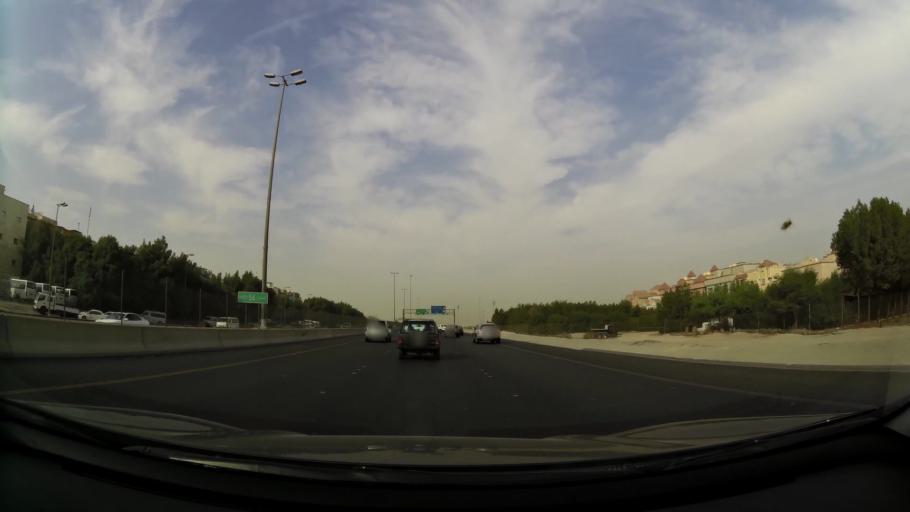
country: KW
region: Al Farwaniyah
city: Al Farwaniyah
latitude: 29.2670
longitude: 47.9328
